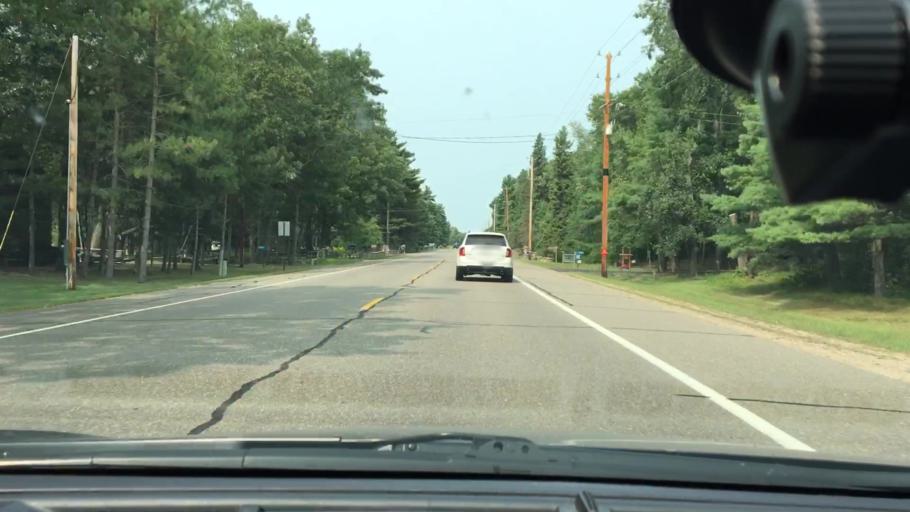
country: US
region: Minnesota
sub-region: Crow Wing County
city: Cross Lake
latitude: 46.5872
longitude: -94.1315
